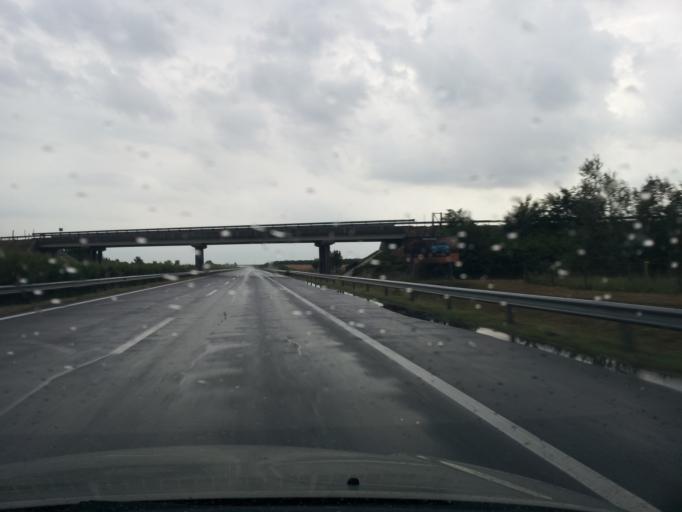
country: HU
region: Borsod-Abauj-Zemplen
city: Nyekladhaza
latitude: 47.9463
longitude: 20.8768
